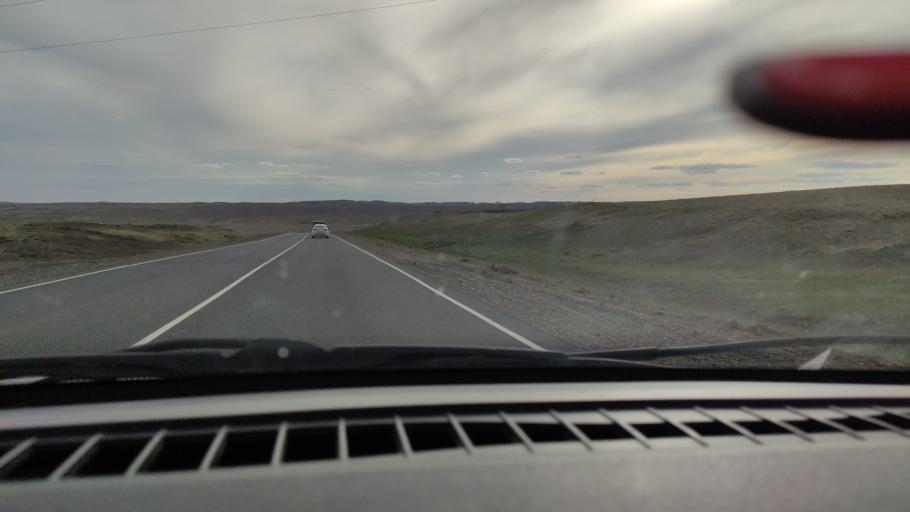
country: RU
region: Bashkortostan
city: Yermolayevo
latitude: 52.6705
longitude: 55.8402
